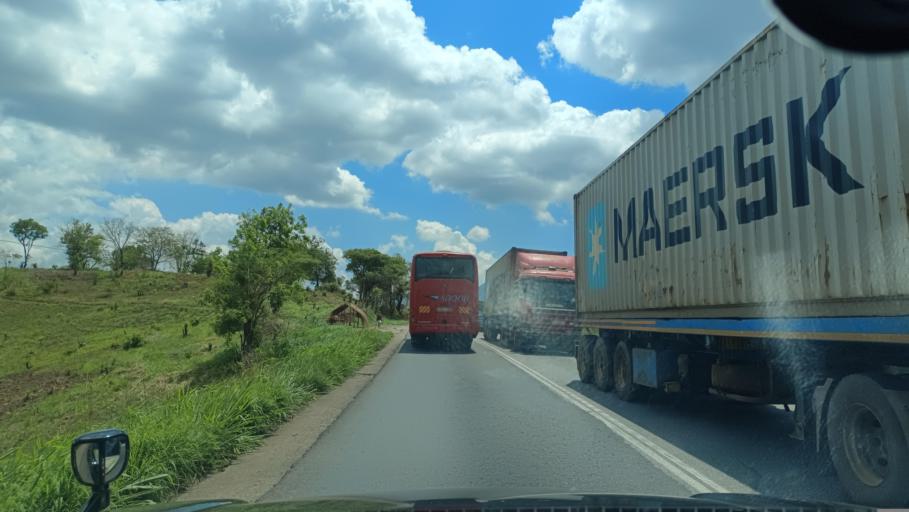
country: TZ
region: Morogoro
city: Mikumi
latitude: -7.4573
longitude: 36.9202
